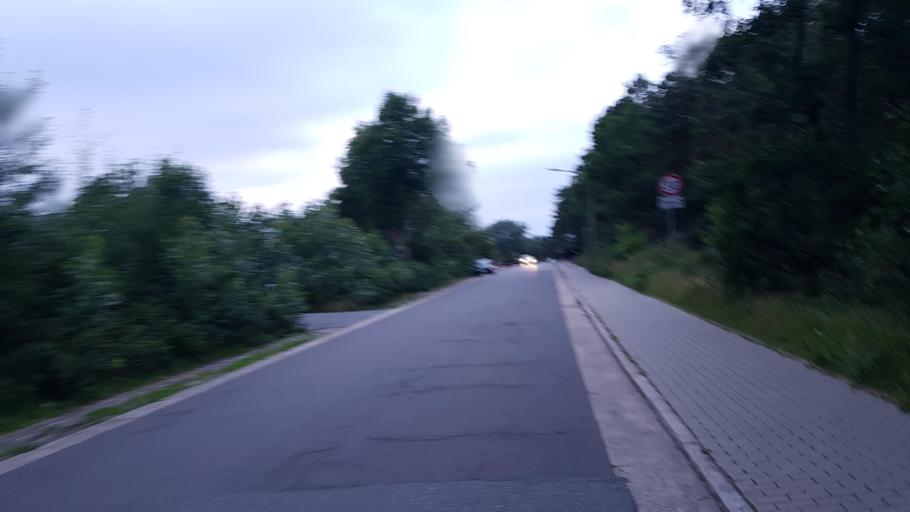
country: DE
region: Schleswig-Holstein
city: Sankt Peter-Ording
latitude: 54.3069
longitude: 8.6221
